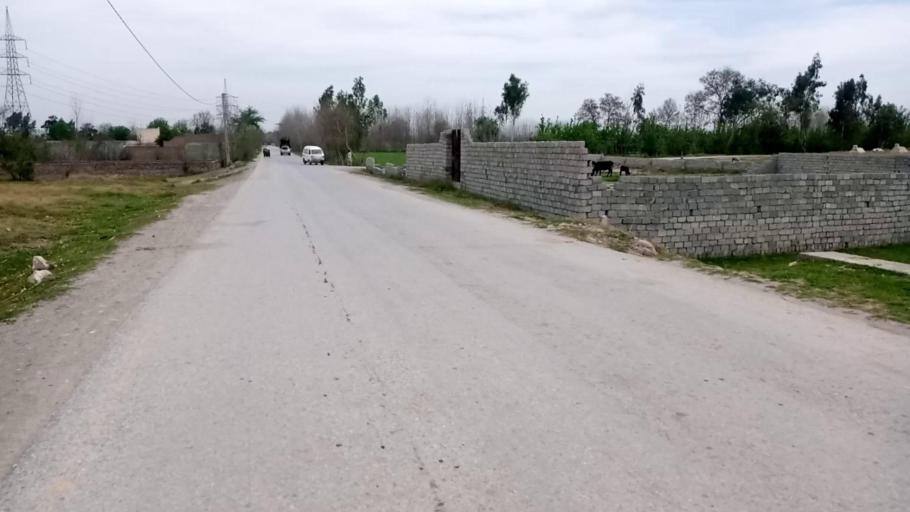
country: PK
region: Khyber Pakhtunkhwa
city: Charsadda
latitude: 34.0633
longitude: 71.6910
